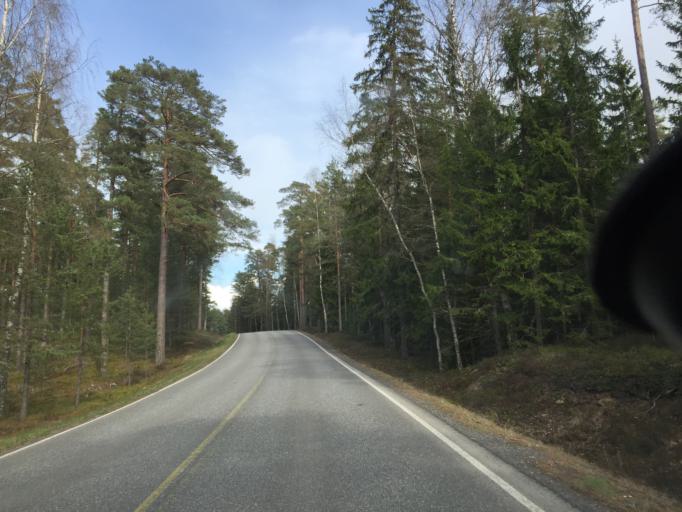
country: FI
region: Varsinais-Suomi
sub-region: Salo
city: Saerkisalo
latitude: 60.0005
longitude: 23.0840
